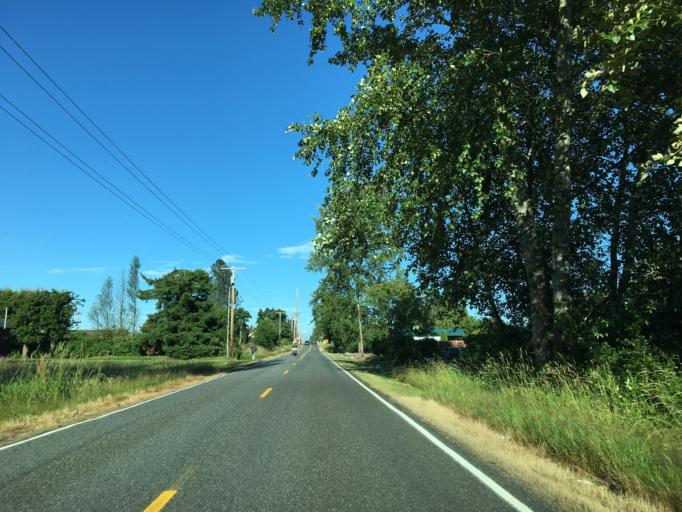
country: US
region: Washington
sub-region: Whatcom County
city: Birch Bay
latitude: 48.9068
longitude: -122.7305
